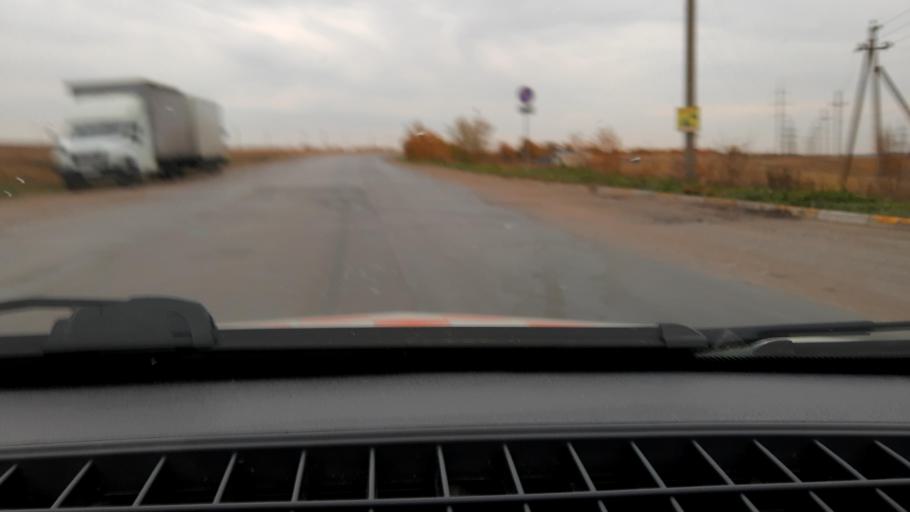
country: RU
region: Bashkortostan
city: Iglino
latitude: 54.7645
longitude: 56.2622
